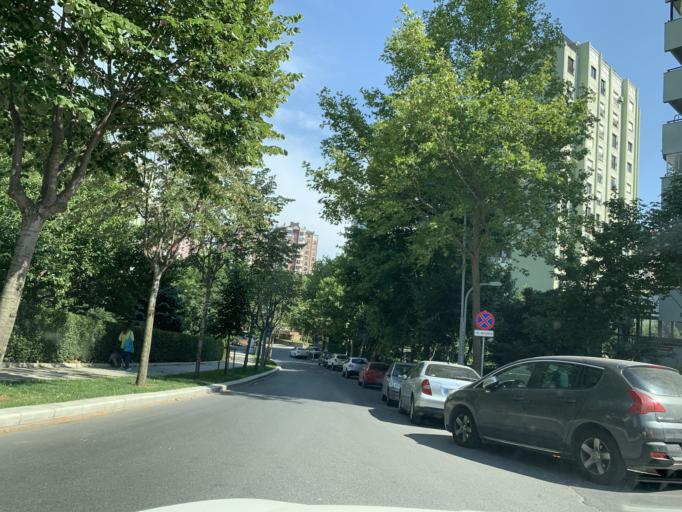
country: TR
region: Istanbul
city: Esenyurt
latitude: 41.0671
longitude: 28.6776
